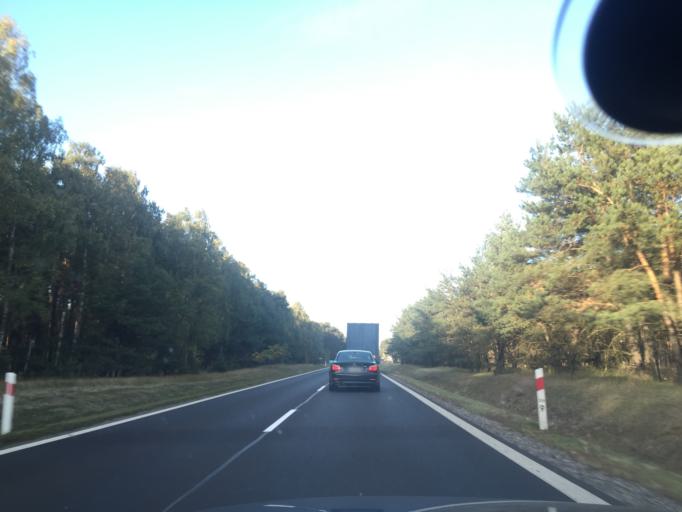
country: PL
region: Kujawsko-Pomorskie
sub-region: Powiat torunski
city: Wielka Nieszawka
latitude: 52.9505
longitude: 18.5273
